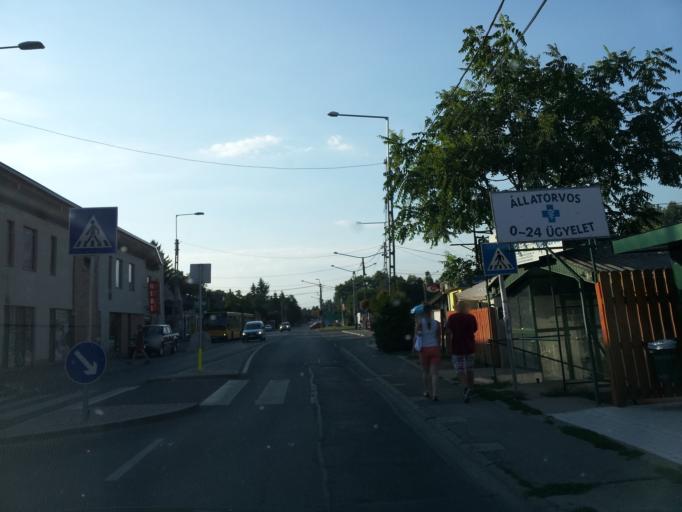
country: HU
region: Pest
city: Tahitotfalu
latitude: 47.7513
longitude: 19.0787
